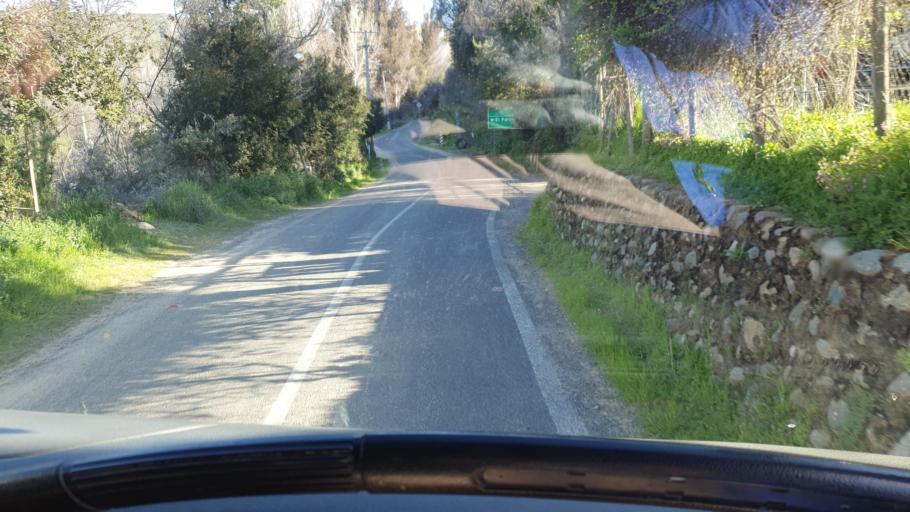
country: CL
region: Valparaiso
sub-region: Provincia de Marga Marga
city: Limache
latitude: -33.1762
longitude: -71.1700
